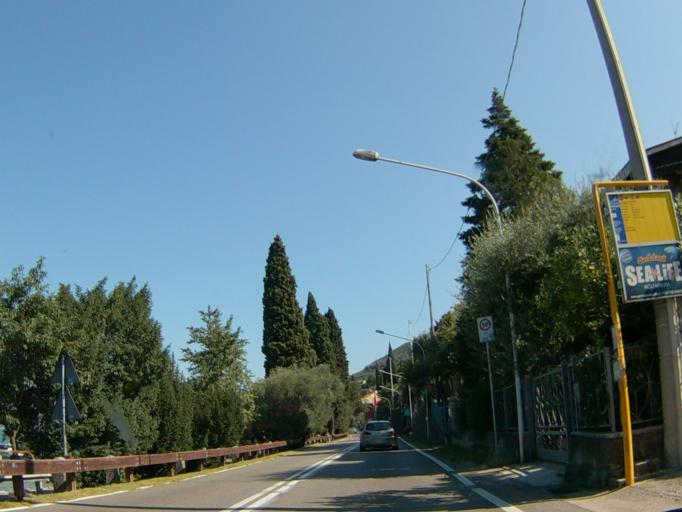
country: IT
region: Veneto
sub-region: Provincia di Verona
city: San Zeno di Montagna
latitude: 45.6498
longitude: 10.7197
